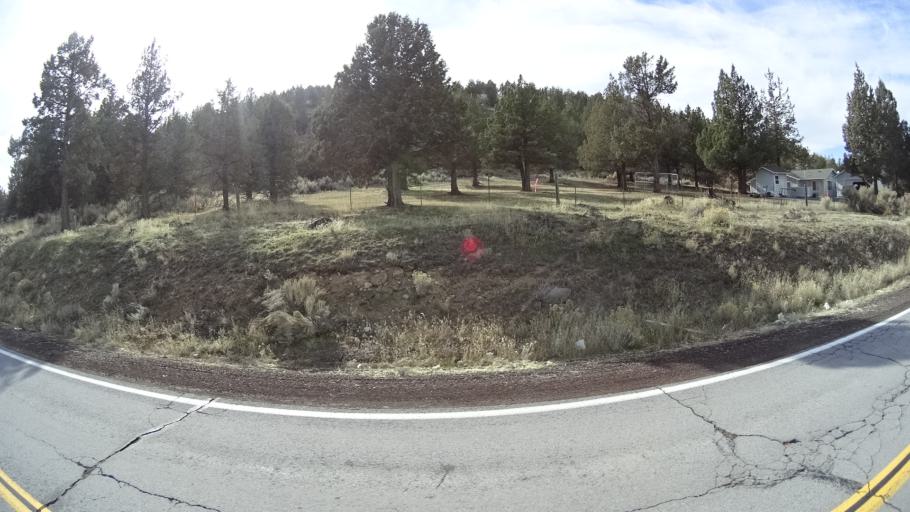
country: US
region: California
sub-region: Siskiyou County
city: Weed
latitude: 41.5413
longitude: -122.3665
